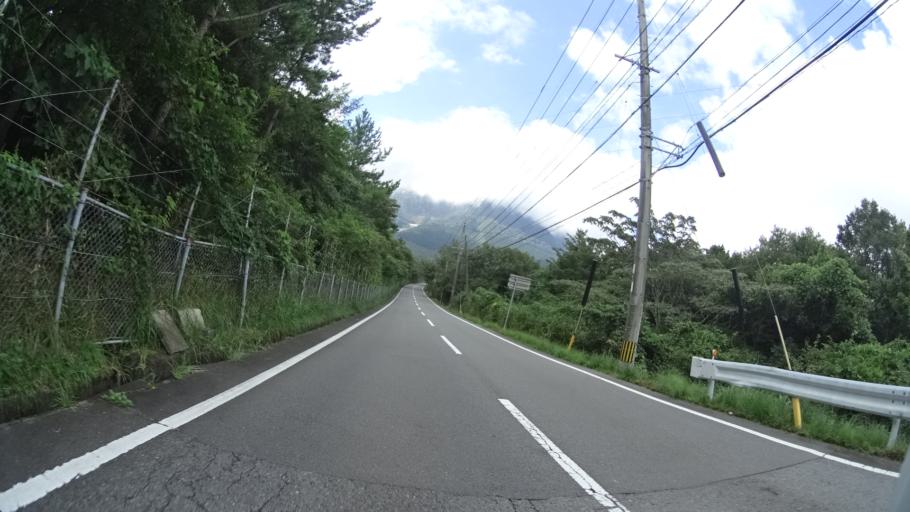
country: JP
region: Oita
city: Beppu
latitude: 33.3096
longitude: 131.4065
